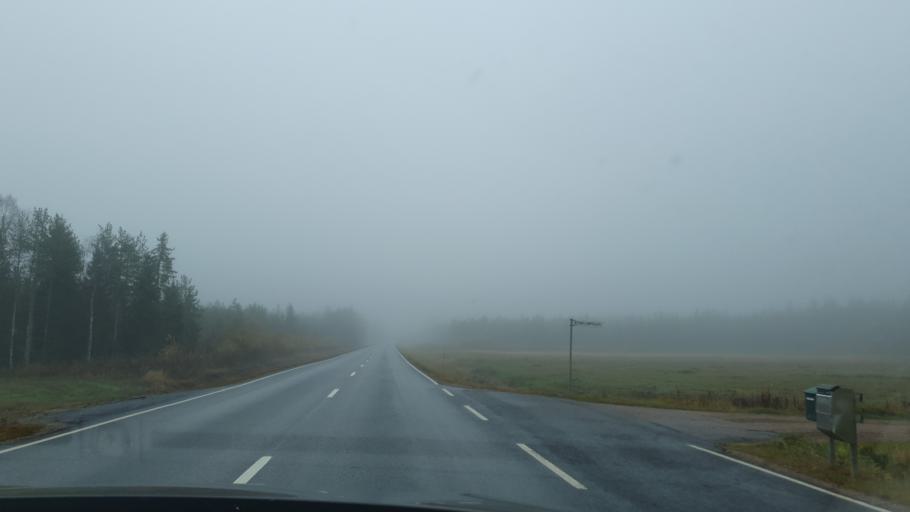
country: FI
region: Lapland
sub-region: Rovaniemi
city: Rovaniemi
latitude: 66.7990
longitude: 25.4143
